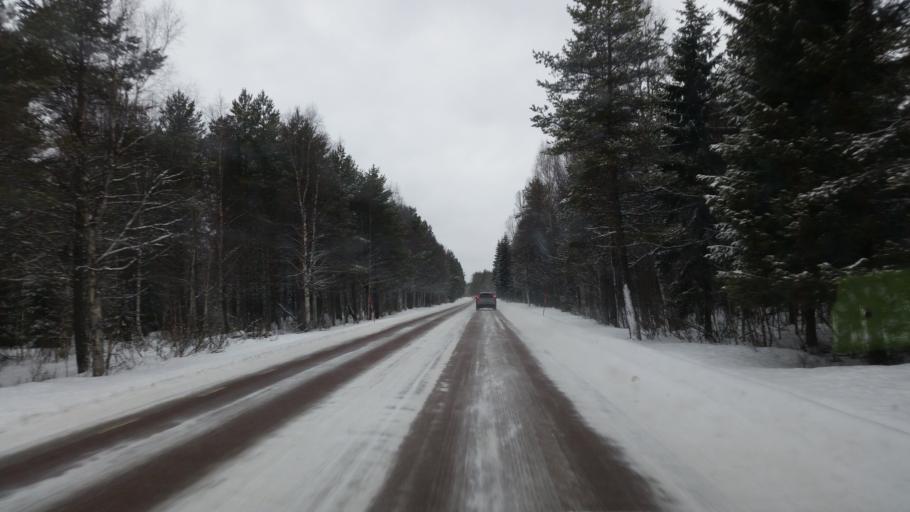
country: SE
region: Jaemtland
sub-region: Harjedalens Kommun
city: Sveg
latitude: 62.3738
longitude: 14.6759
